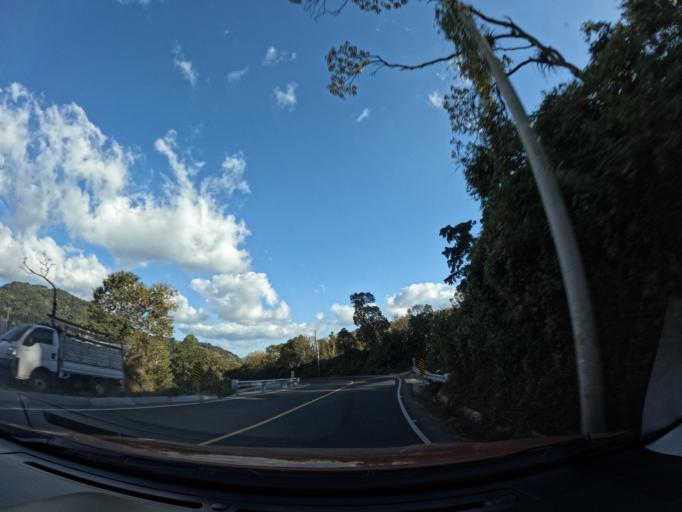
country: GT
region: Sacatepequez
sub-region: Municipio de Santa Maria de Jesus
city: Santa Maria de Jesus
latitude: 14.4806
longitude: -90.7014
